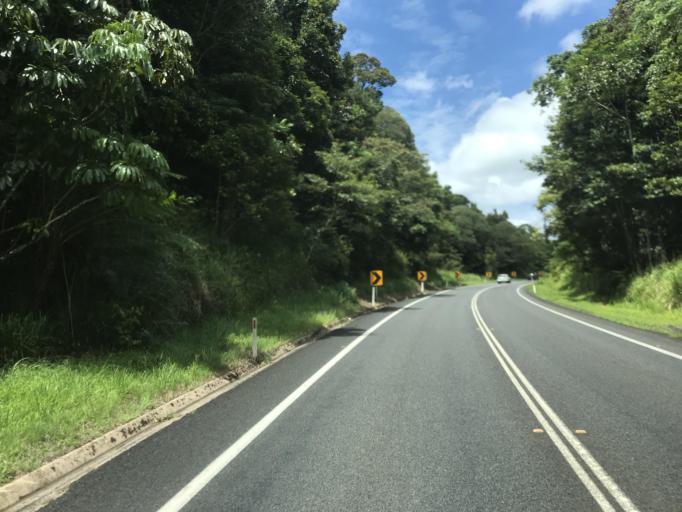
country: AU
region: Queensland
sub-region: Tablelands
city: Ravenshoe
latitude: -17.5948
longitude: 145.7455
